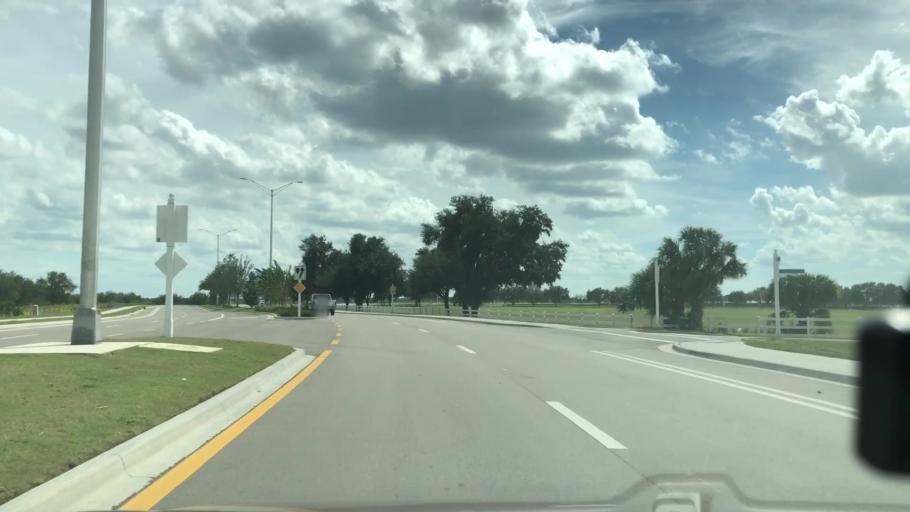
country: US
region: Florida
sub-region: Sarasota County
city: The Meadows
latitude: 27.3839
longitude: -82.3980
